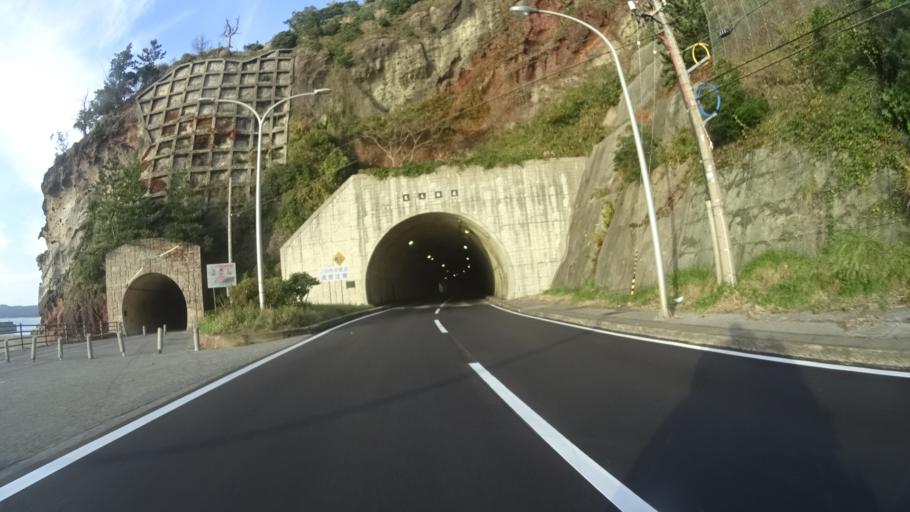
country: JP
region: Ishikawa
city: Nanao
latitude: 37.1319
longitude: 136.7271
